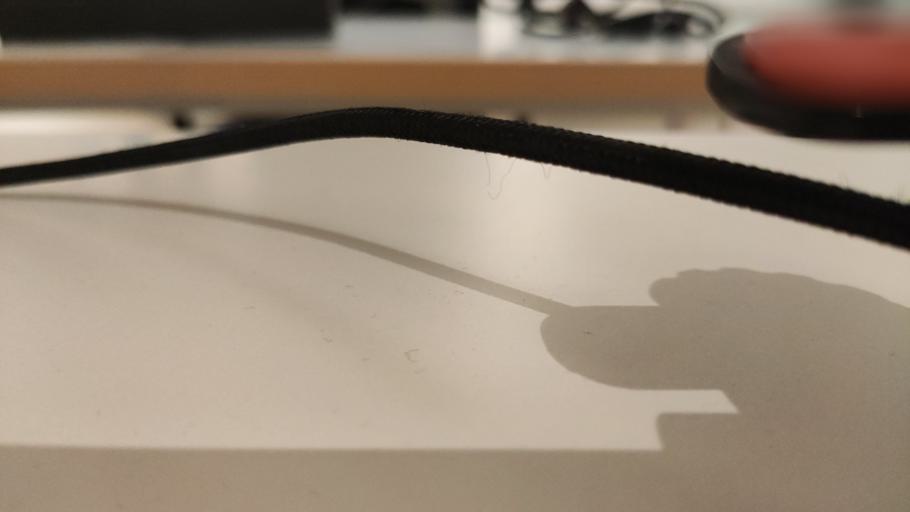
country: RU
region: Moskovskaya
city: Dorokhovo
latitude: 55.4578
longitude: 36.3535
